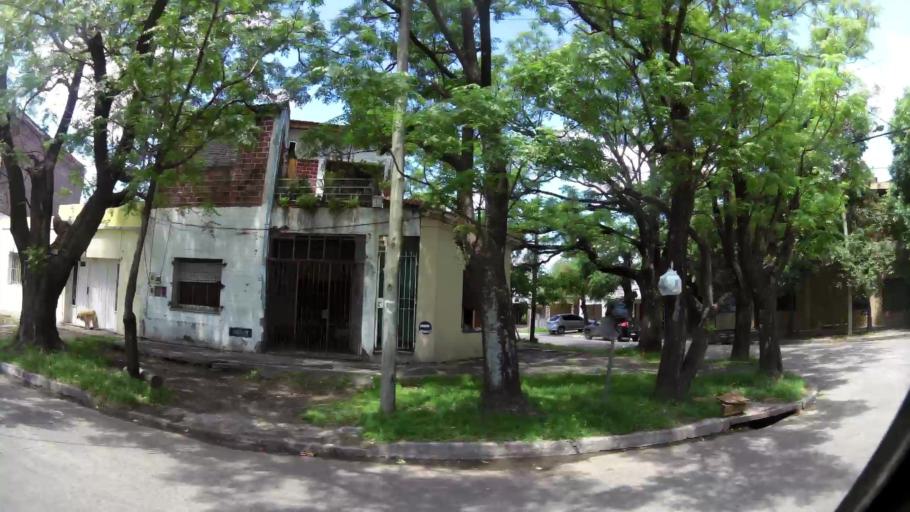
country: AR
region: Buenos Aires
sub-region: Partido de Lomas de Zamora
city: Lomas de Zamora
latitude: -34.7338
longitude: -58.4140
